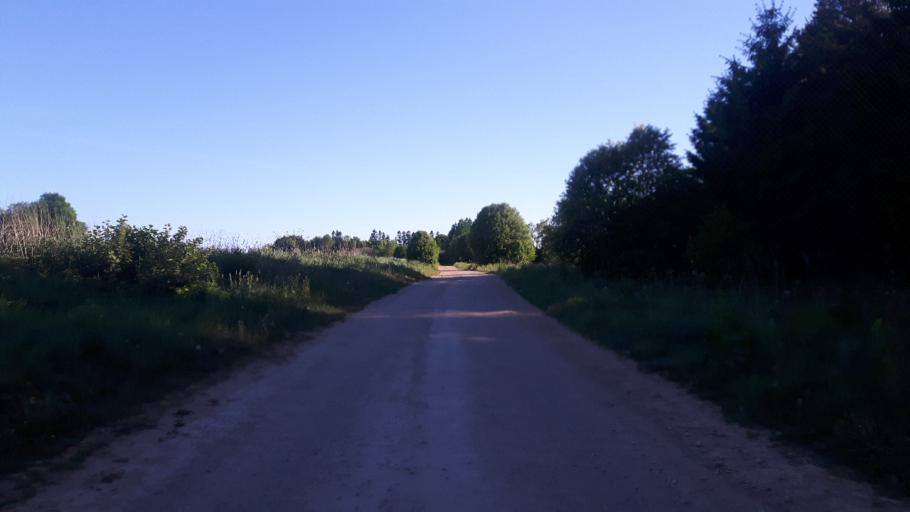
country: EE
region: Ida-Virumaa
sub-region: Puessi linn
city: Pussi
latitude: 59.4221
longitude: 27.0640
